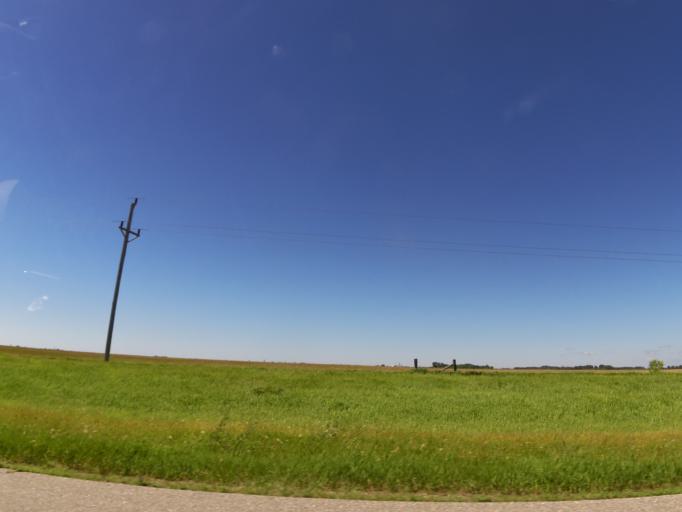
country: US
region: Minnesota
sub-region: Red Lake County
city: Red Lake Falls
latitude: 47.7441
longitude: -96.2308
